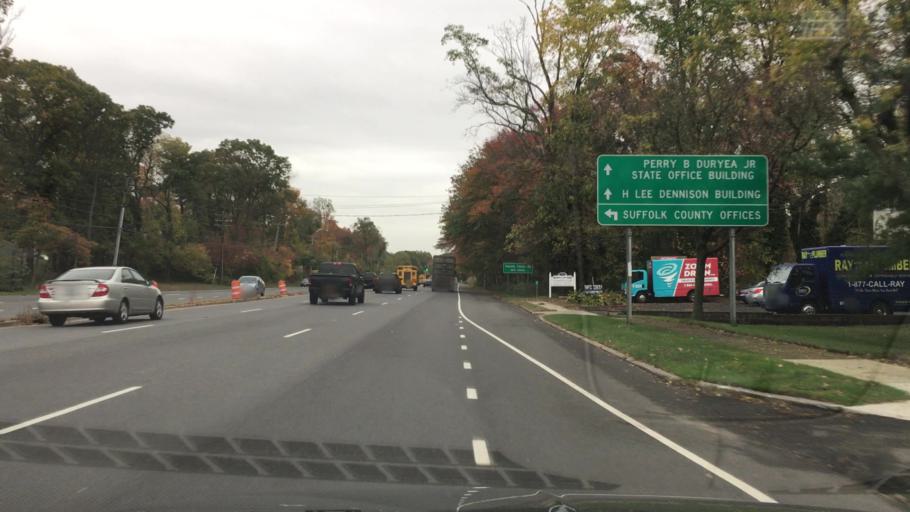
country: US
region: New York
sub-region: Suffolk County
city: Hauppauge
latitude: 40.8249
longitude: -73.2337
